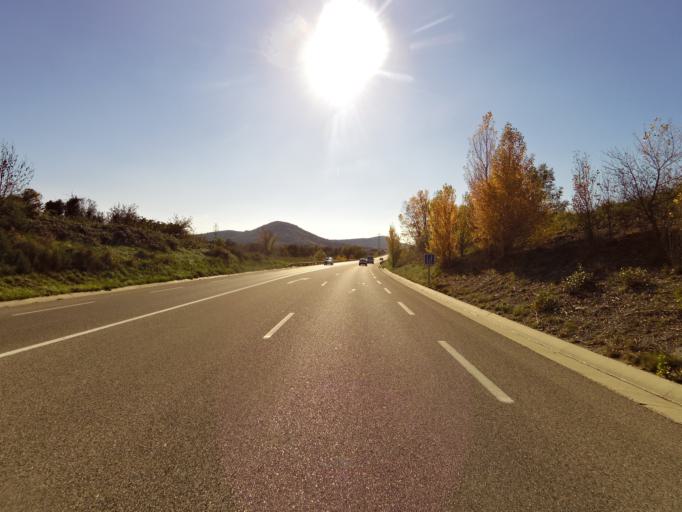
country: FR
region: Rhone-Alpes
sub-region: Departement de l'Ardeche
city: Saint-Sernin
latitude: 44.5841
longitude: 4.3848
